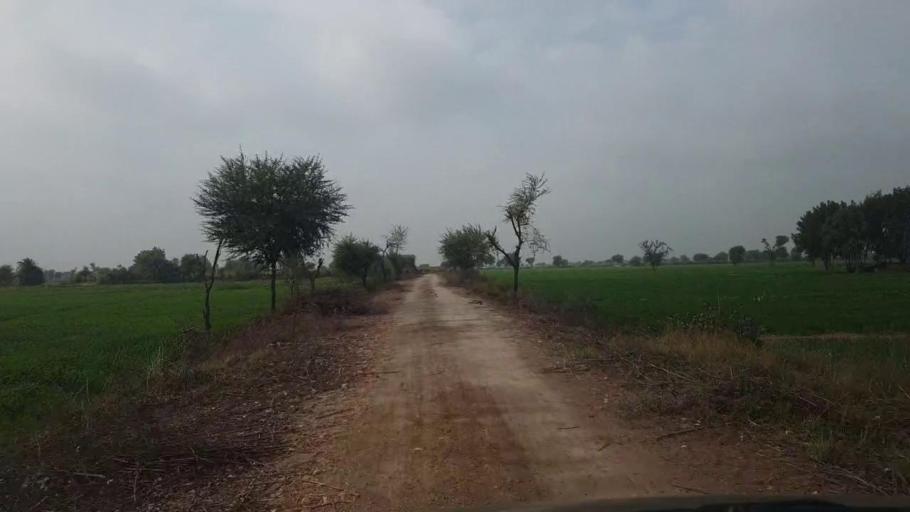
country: PK
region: Sindh
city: Shahdadpur
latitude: 25.9635
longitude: 68.7118
